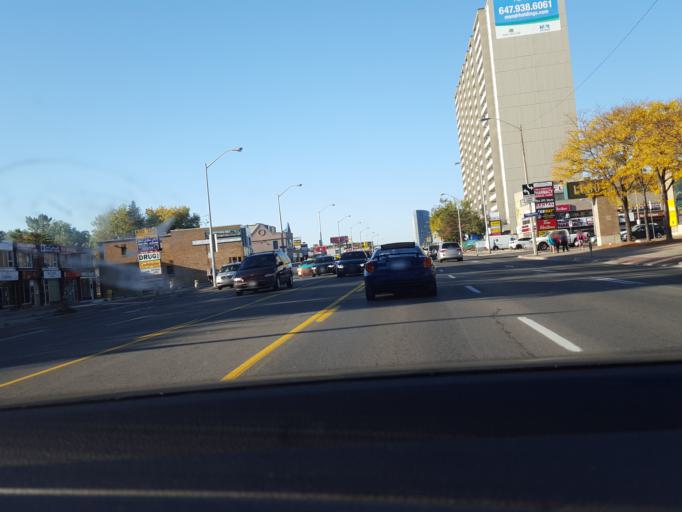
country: CA
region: Ontario
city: North York
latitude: 43.7883
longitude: -79.4176
